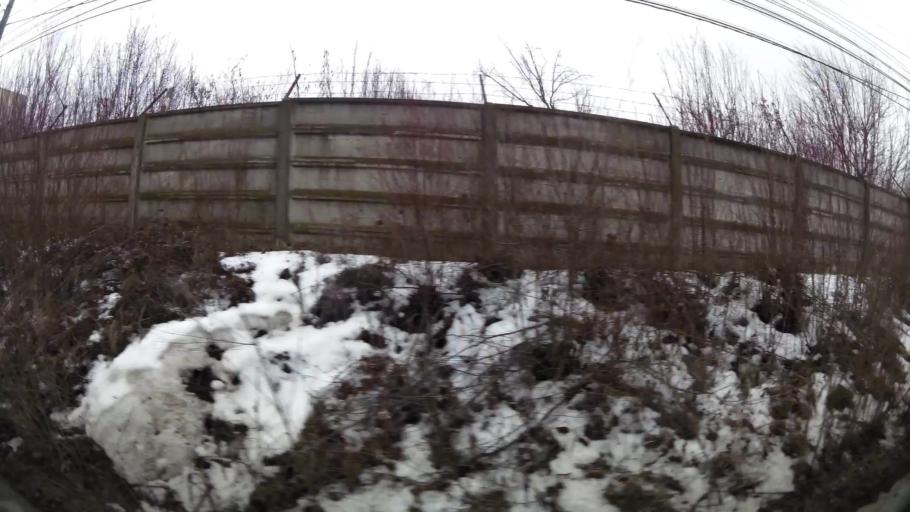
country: RO
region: Ilfov
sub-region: Comuna Chitila
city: Chitila
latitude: 44.4971
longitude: 26.0065
